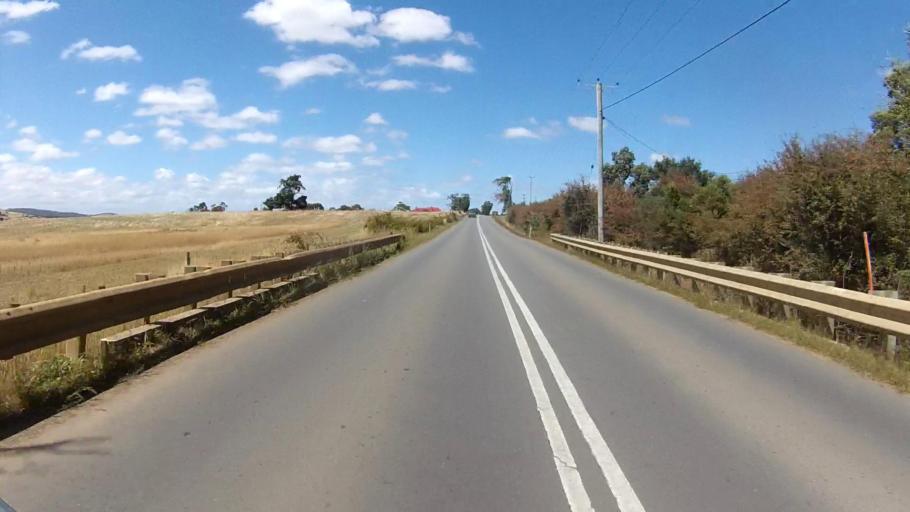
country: AU
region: Tasmania
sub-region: Clarence
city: Cambridge
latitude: -42.7734
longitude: 147.4152
